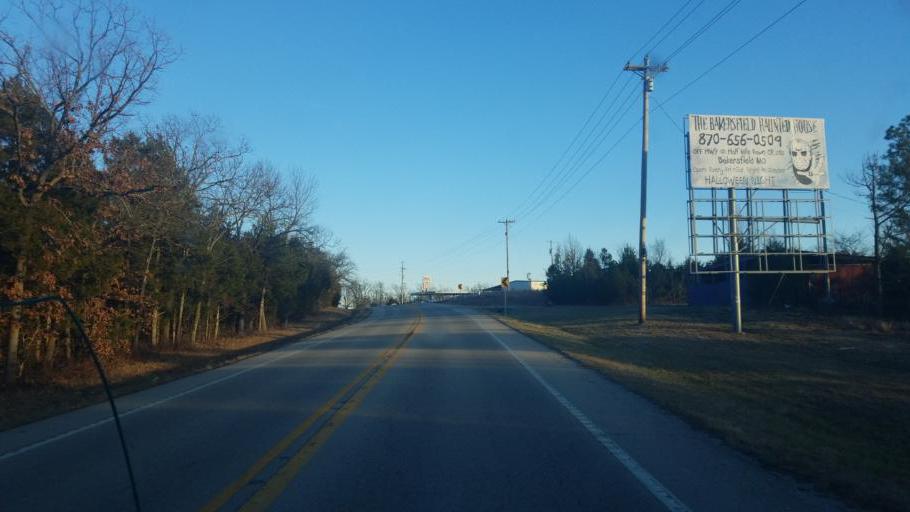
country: US
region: Arkansas
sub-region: Baxter County
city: Mountain Home
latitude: 36.3846
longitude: -92.1752
